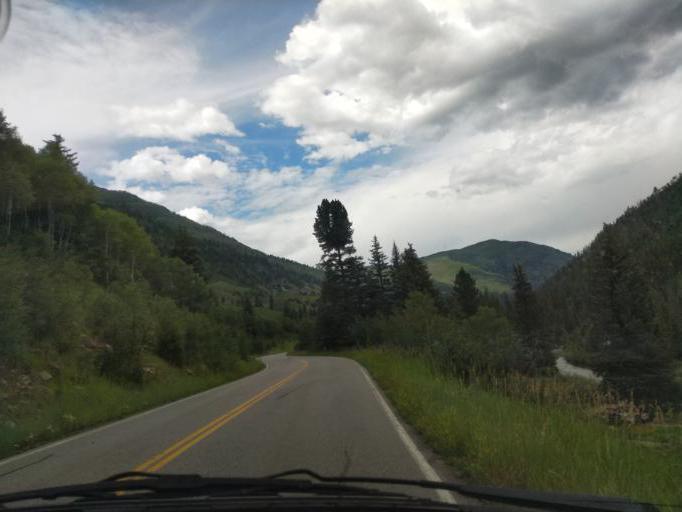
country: US
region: Colorado
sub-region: Garfield County
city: Carbondale
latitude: 39.1005
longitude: -107.2633
